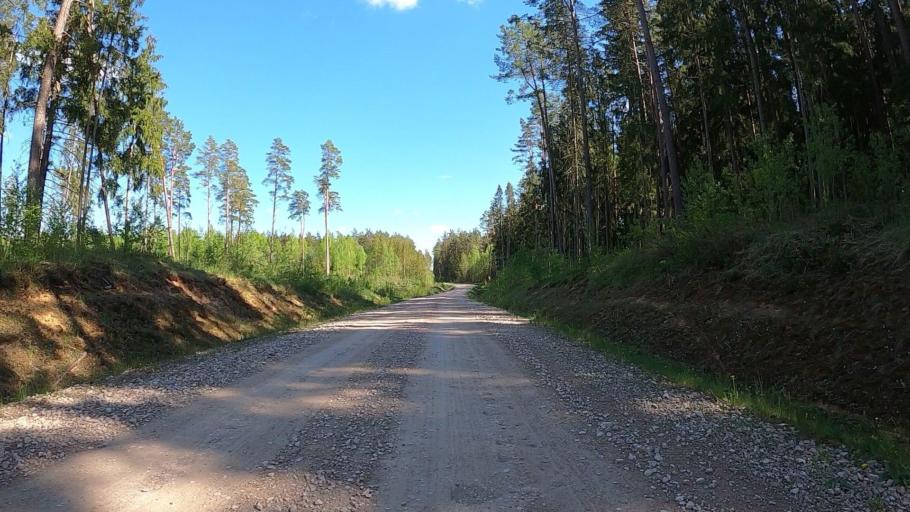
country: LV
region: Baldone
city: Baldone
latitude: 56.7679
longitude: 24.3773
